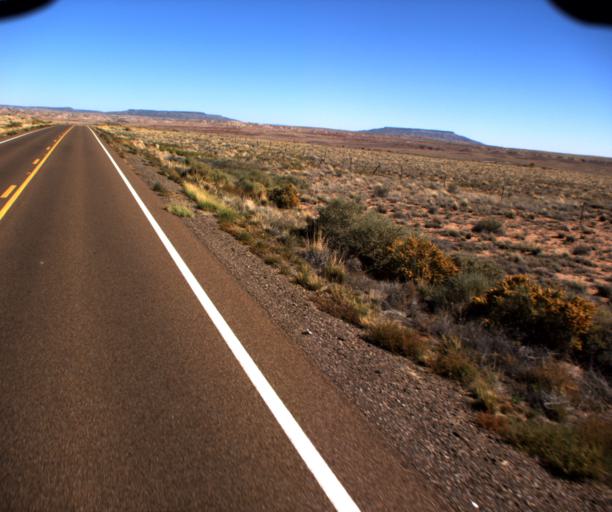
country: US
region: Arizona
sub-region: Navajo County
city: Joseph City
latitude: 35.1580
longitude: -110.4620
